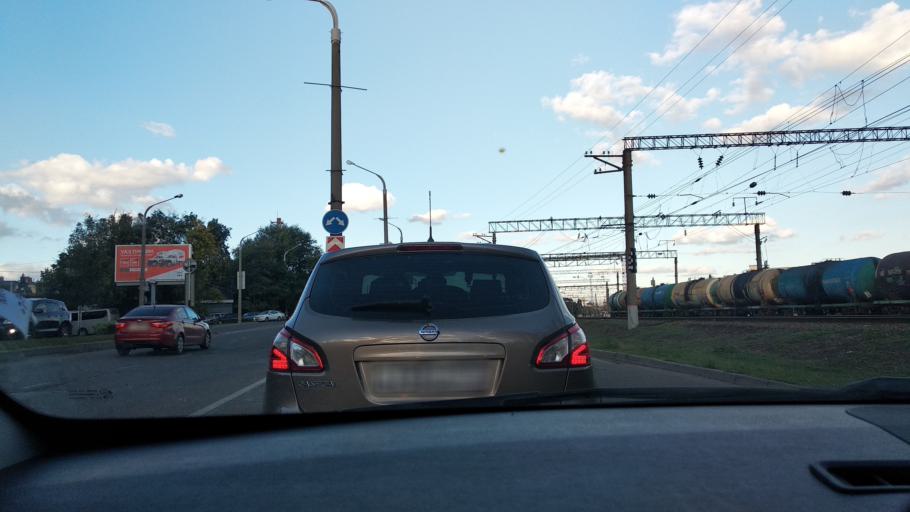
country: RU
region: Krasnodarskiy
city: Krasnodar
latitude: 45.0119
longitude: 38.9736
